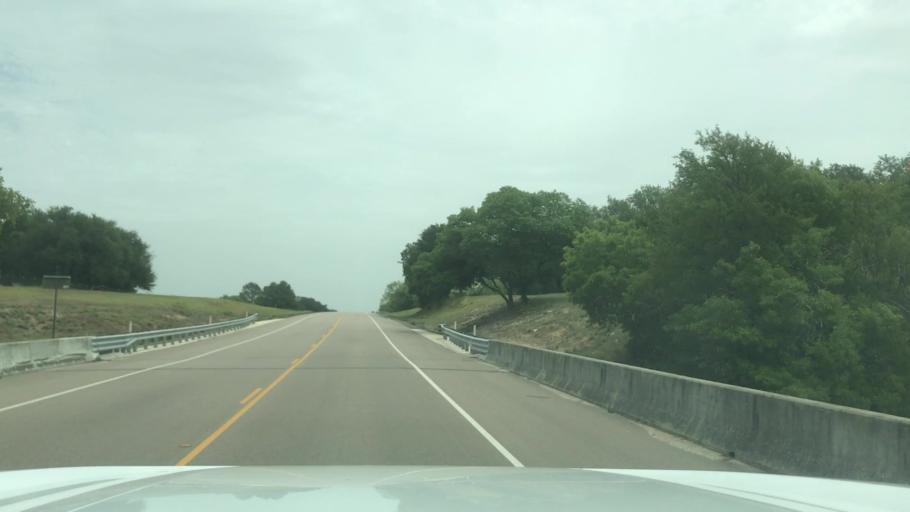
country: US
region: Texas
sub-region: Hamilton County
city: Hico
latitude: 31.9776
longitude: -97.8950
